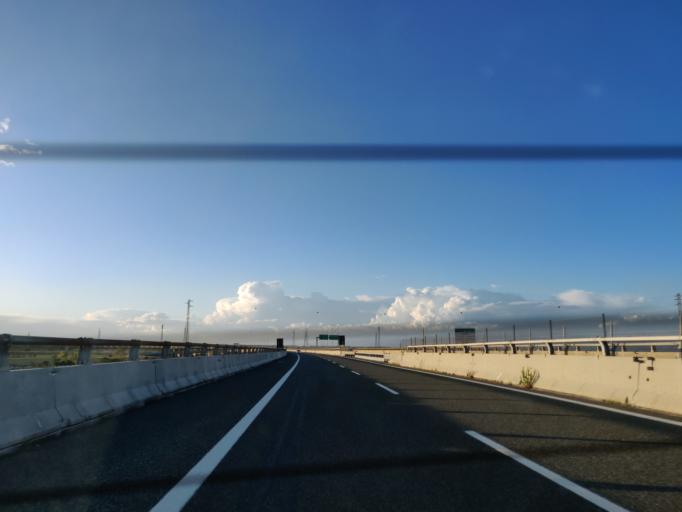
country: IT
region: Tuscany
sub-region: Provincia di Livorno
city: Vicarello
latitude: 43.6080
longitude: 10.4447
